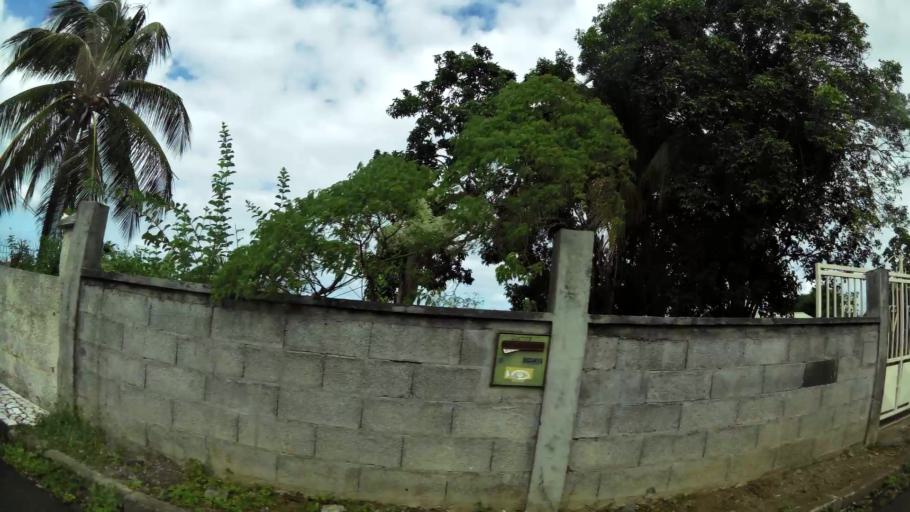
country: GP
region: Guadeloupe
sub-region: Guadeloupe
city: Sainte-Rose
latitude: 16.3329
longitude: -61.6932
